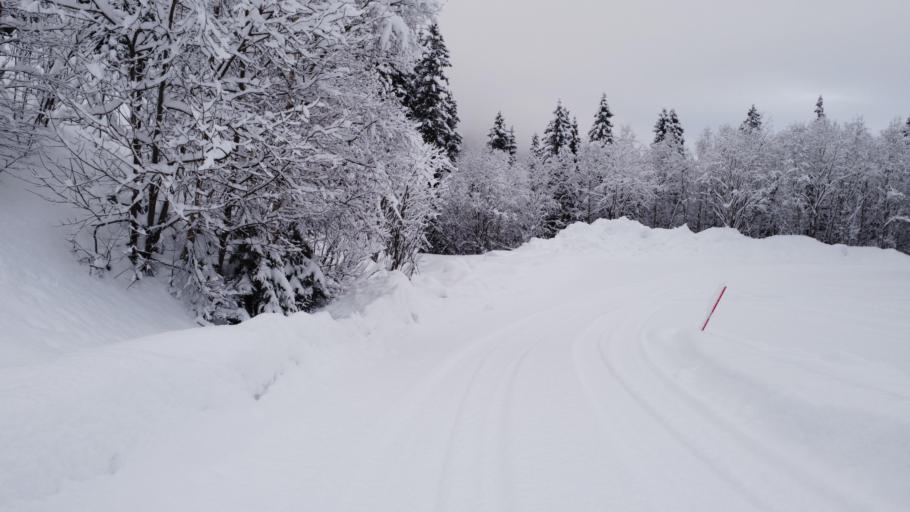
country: NO
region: Nordland
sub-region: Rana
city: Mo i Rana
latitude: 66.3329
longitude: 14.1595
